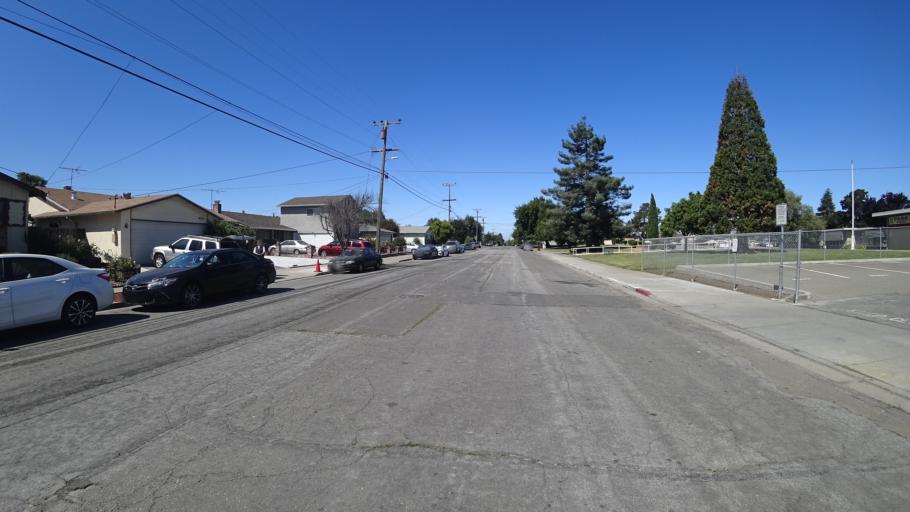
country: US
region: California
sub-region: Alameda County
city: Hayward
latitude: 37.6533
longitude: -122.0927
